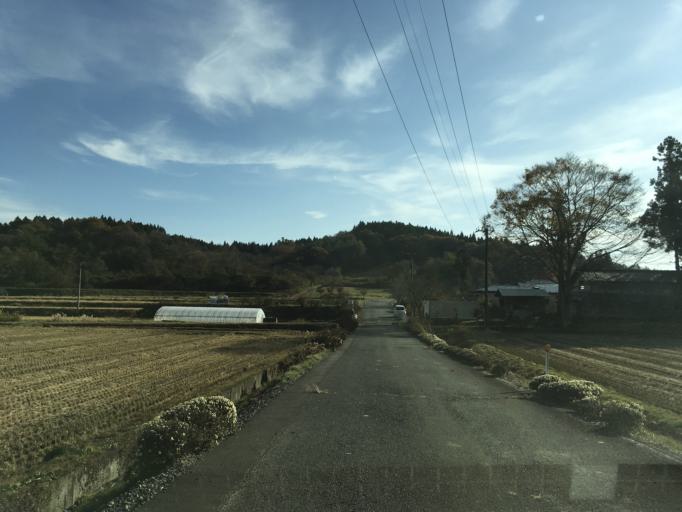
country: JP
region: Iwate
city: Ichinoseki
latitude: 38.8072
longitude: 141.1529
